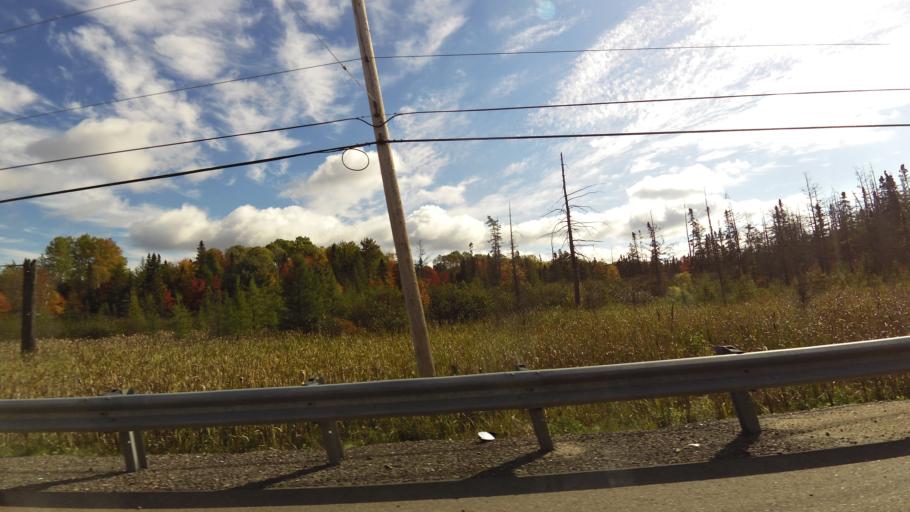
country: CA
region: Ontario
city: Deep River
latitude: 46.0594
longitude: -77.4749
